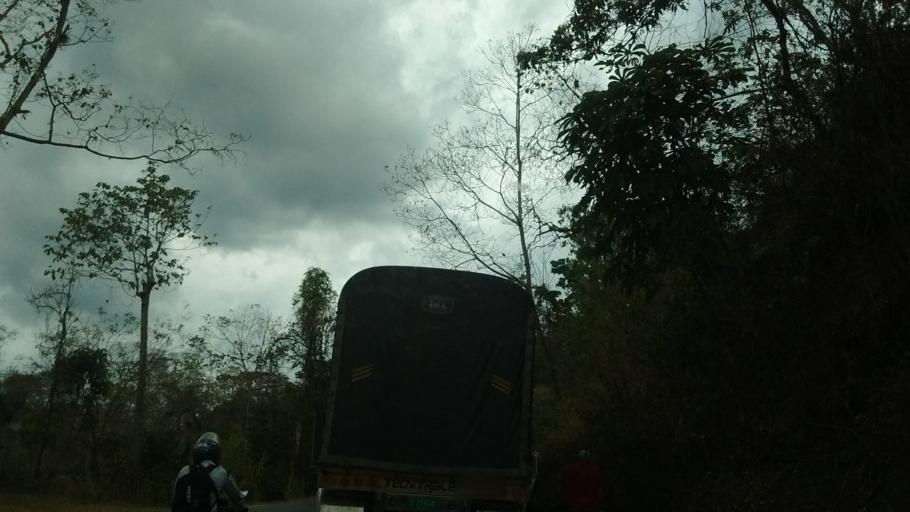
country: CO
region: Cauca
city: Rosas
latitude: 2.2771
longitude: -76.7224
